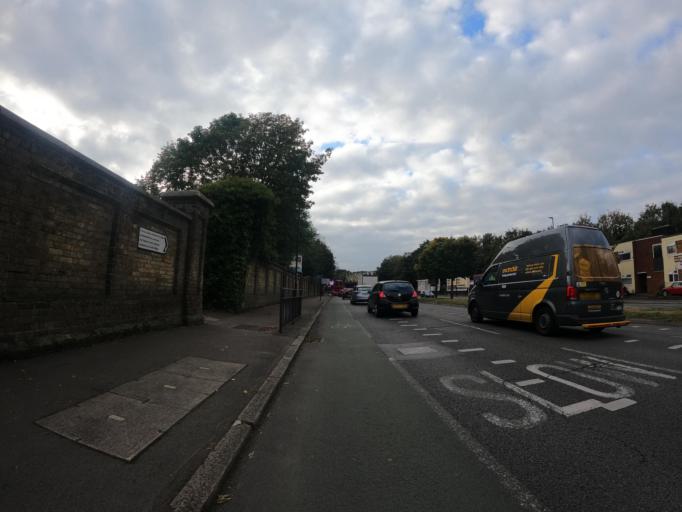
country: GB
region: England
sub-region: Greater London
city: Southall
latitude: 51.5090
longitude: -0.3522
